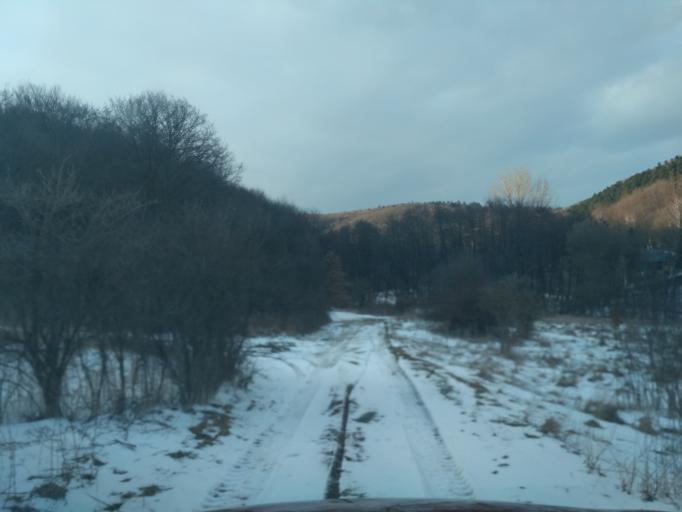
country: SK
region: Kosicky
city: Kosice
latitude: 48.7449
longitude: 21.1504
